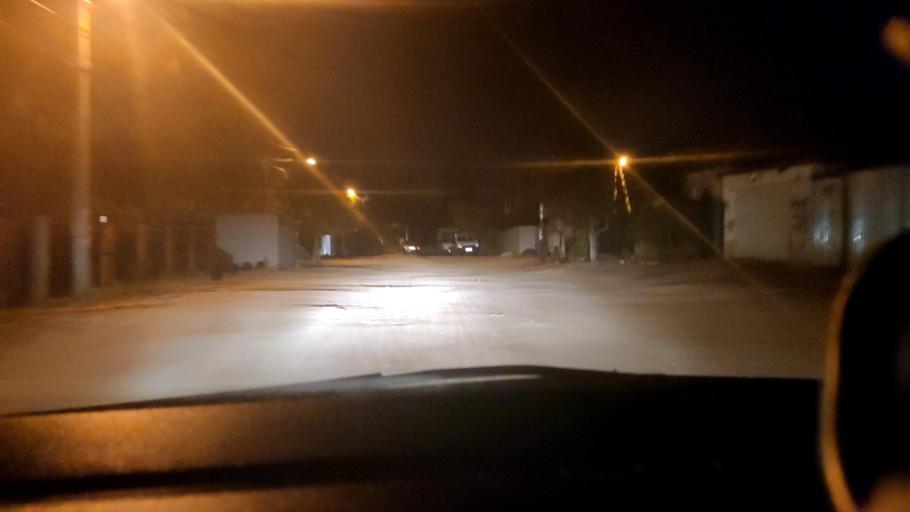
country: RU
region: Voronezj
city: Maslovka
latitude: 51.6149
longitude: 39.2323
